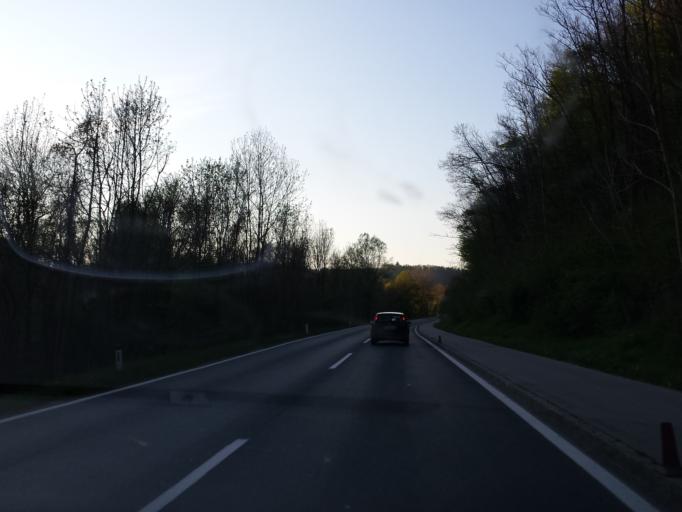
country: AT
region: Styria
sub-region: Graz Stadt
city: Goesting
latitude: 47.1137
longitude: 15.3777
